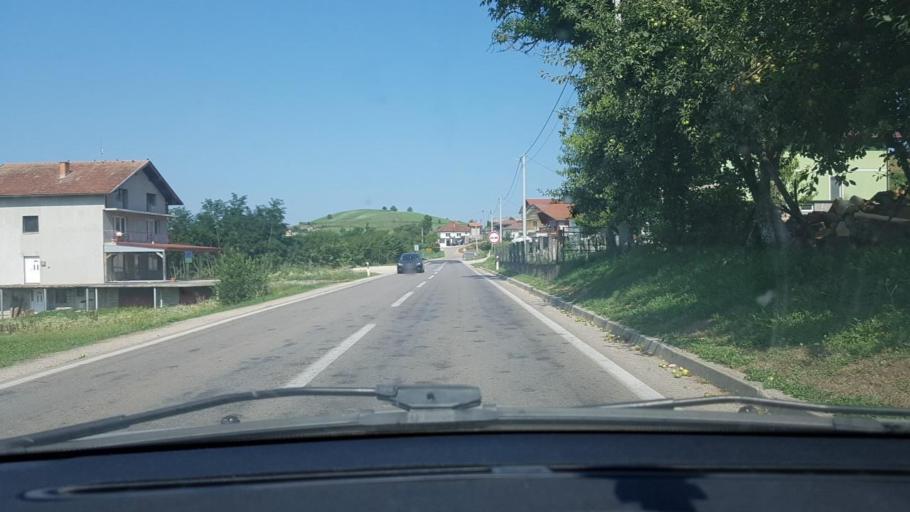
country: BA
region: Federation of Bosnia and Herzegovina
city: Mala Kladusa
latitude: 45.1338
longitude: 15.8541
